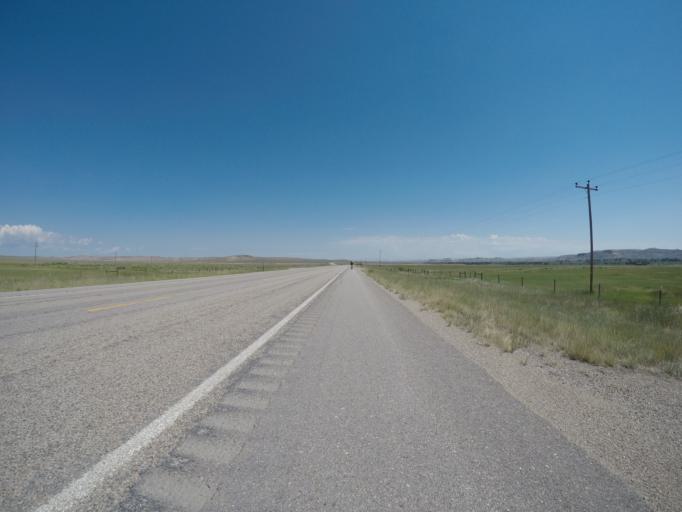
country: US
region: Wyoming
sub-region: Sublette County
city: Marbleton
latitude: 42.4176
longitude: -110.1138
